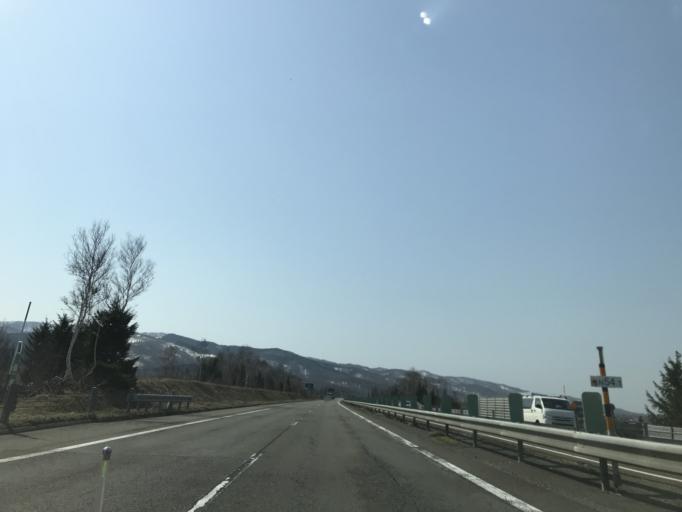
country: JP
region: Hokkaido
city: Bibai
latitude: 43.3422
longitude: 141.8876
